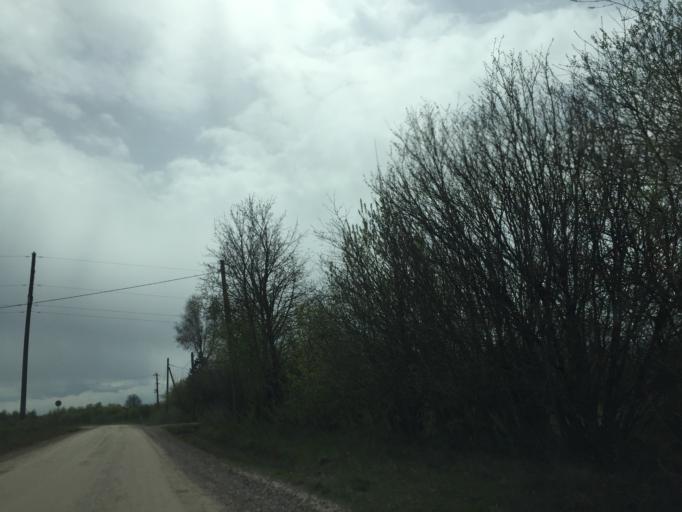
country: LV
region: Lecava
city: Iecava
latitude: 56.6253
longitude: 24.1851
